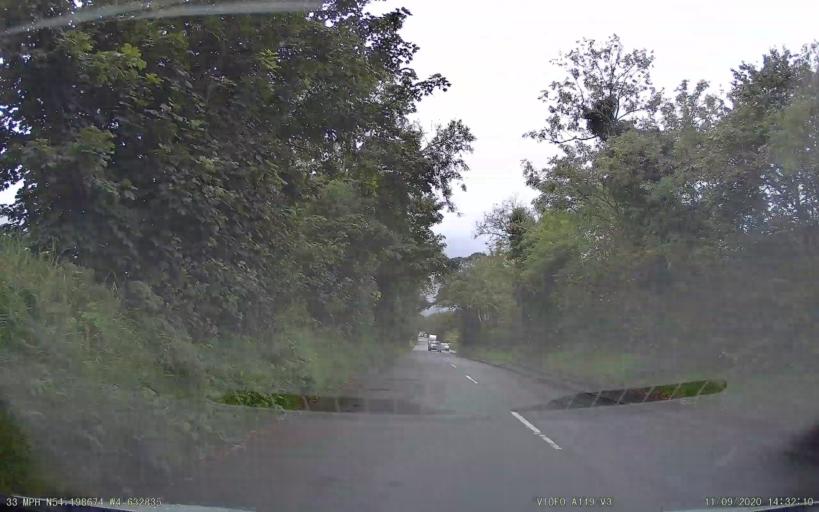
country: IM
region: Castletown
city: Castletown
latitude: 54.1987
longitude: -4.6328
